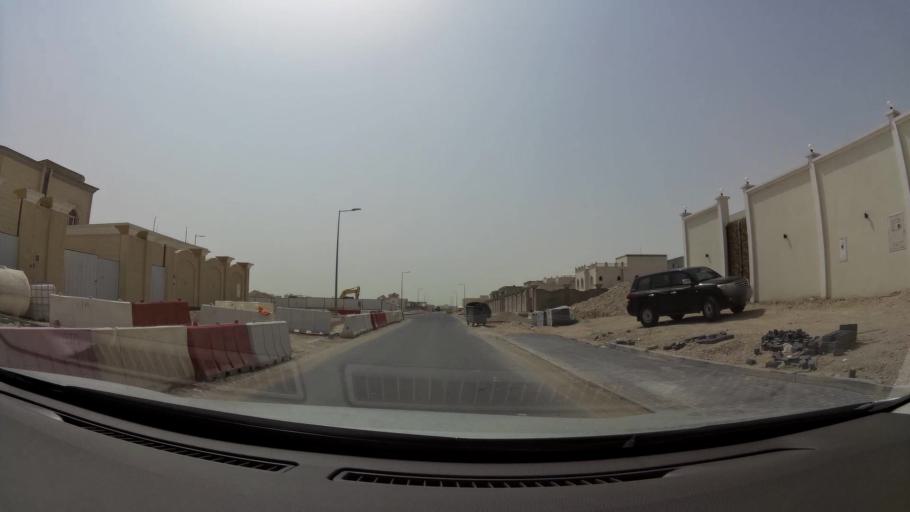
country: QA
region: Baladiyat ar Rayyan
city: Ar Rayyan
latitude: 25.2591
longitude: 51.3691
